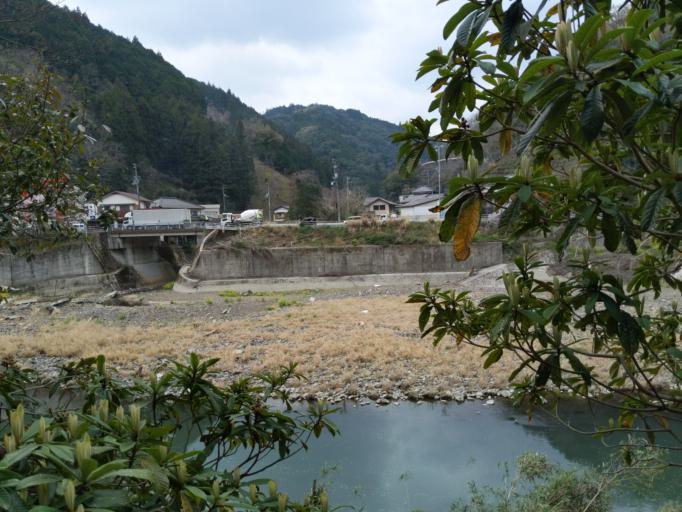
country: JP
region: Ehime
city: Ozu
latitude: 33.4561
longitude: 132.6803
